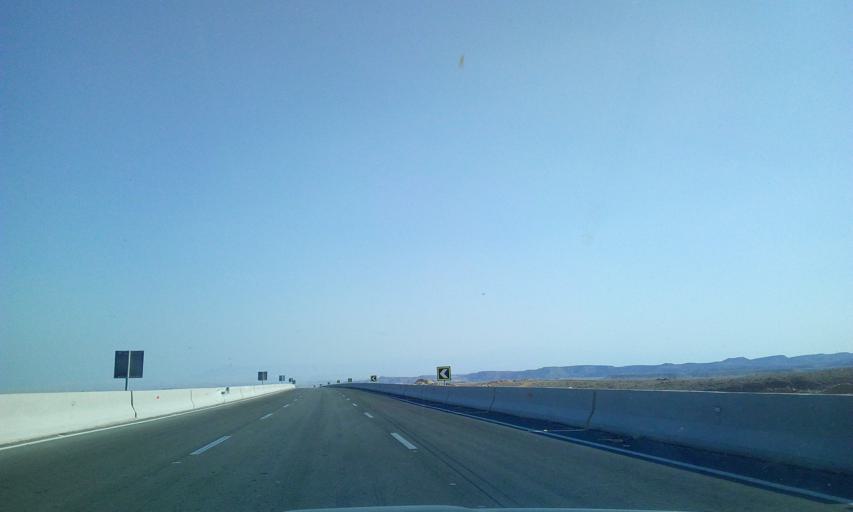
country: EG
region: As Suways
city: Ain Sukhna
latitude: 29.2748
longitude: 32.4694
